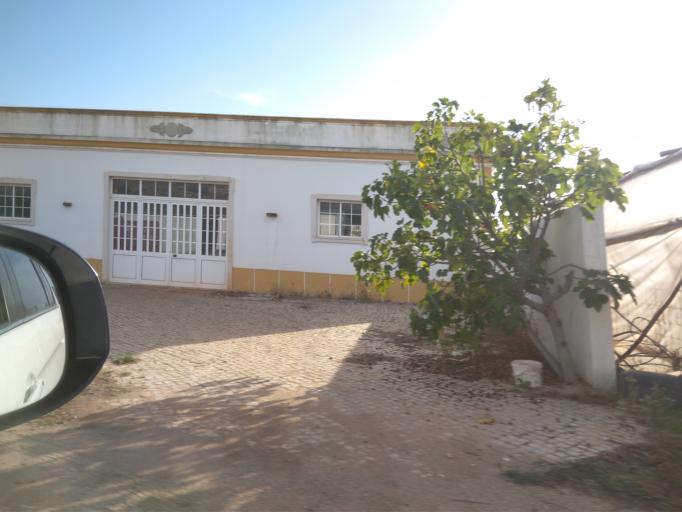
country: PT
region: Faro
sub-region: Faro
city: Santa Barbara de Nexe
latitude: 37.0963
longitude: -7.9510
